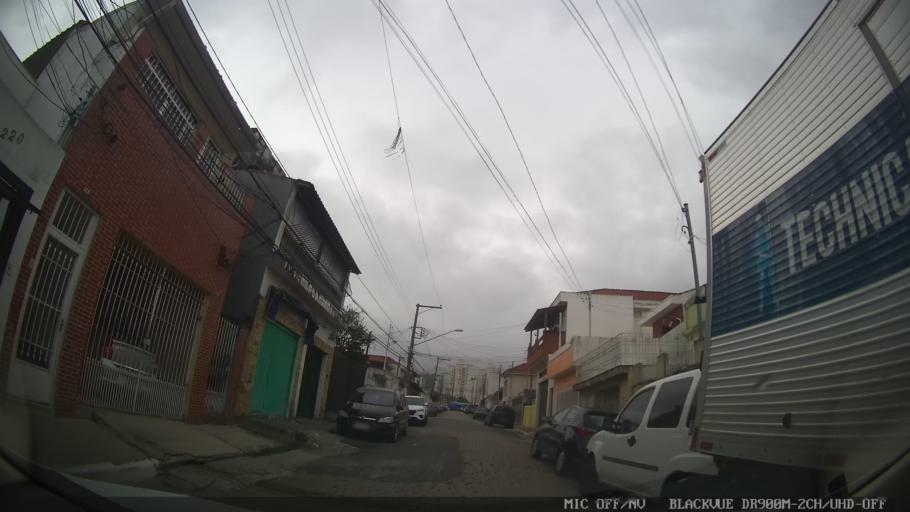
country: BR
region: Sao Paulo
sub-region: Sao Paulo
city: Sao Paulo
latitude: -23.5062
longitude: -46.6135
